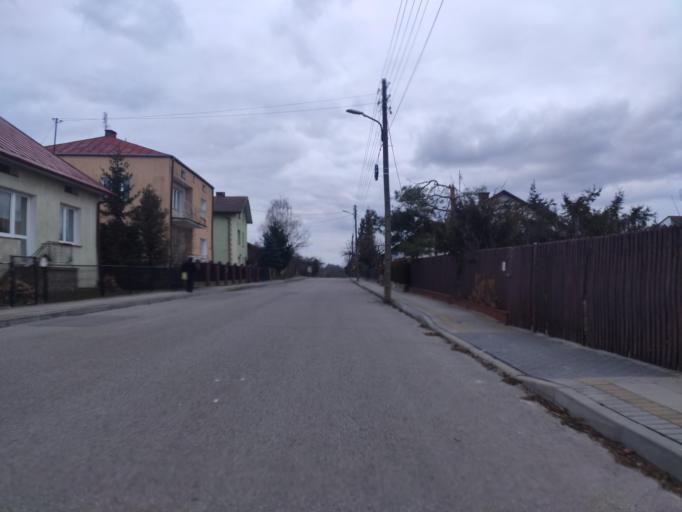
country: PL
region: Lublin Voivodeship
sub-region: Powiat lubartowski
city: Kock
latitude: 51.6387
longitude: 22.4388
